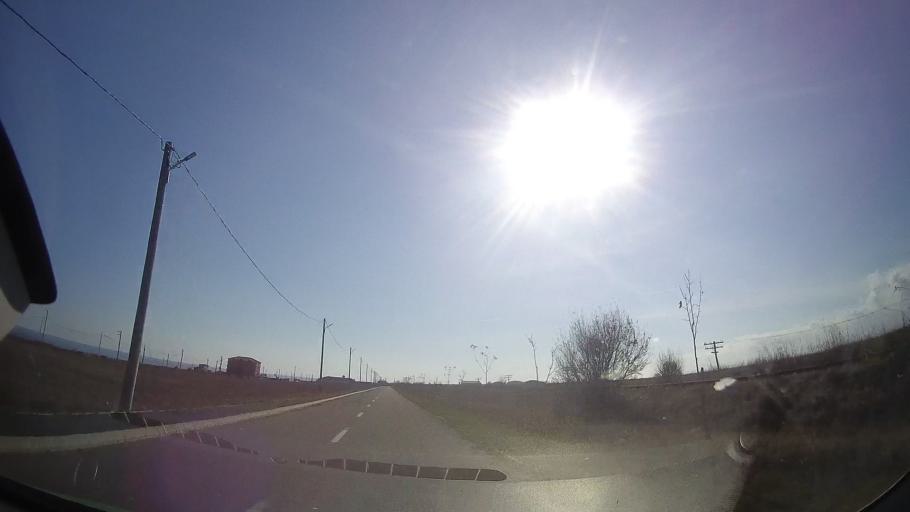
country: RO
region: Constanta
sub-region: Comuna Costinesti
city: Schitu
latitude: 43.9303
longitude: 28.6317
